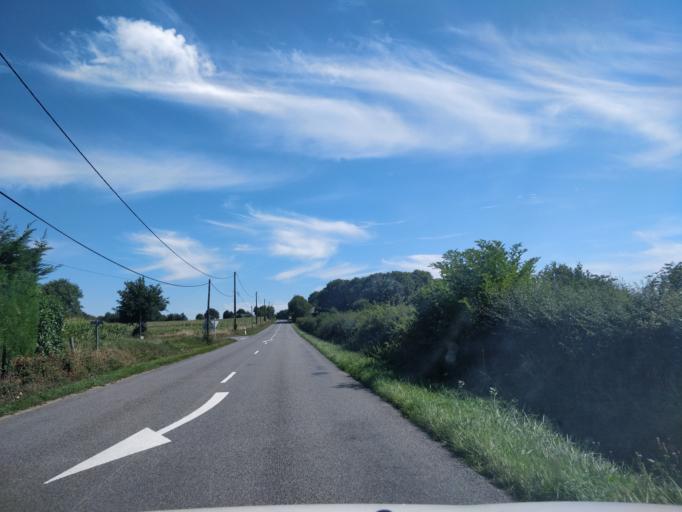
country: FR
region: Pays de la Loire
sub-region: Departement de la Loire-Atlantique
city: Conquereuil
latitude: 47.6773
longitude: -1.7618
